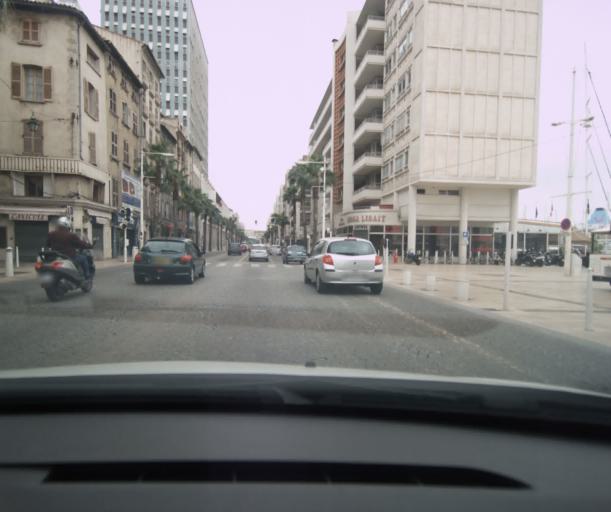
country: FR
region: Provence-Alpes-Cote d'Azur
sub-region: Departement du Var
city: Toulon
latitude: 43.1208
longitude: 5.9312
